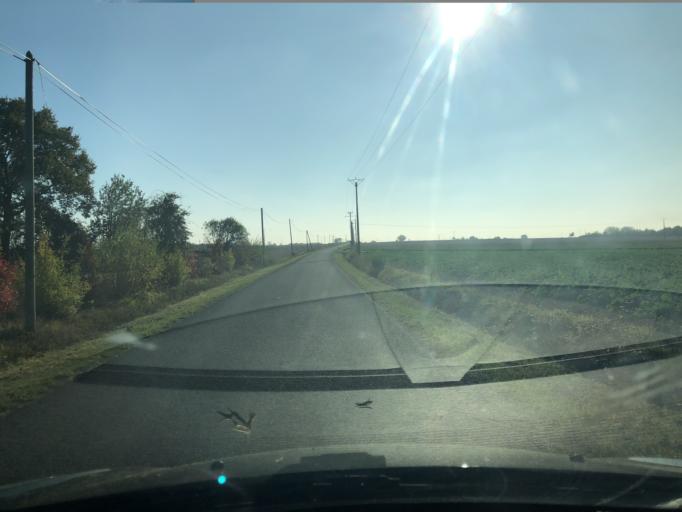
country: FR
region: Centre
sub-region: Departement d'Indre-et-Loire
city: Neuvy-le-Roi
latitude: 47.6382
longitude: 0.6083
